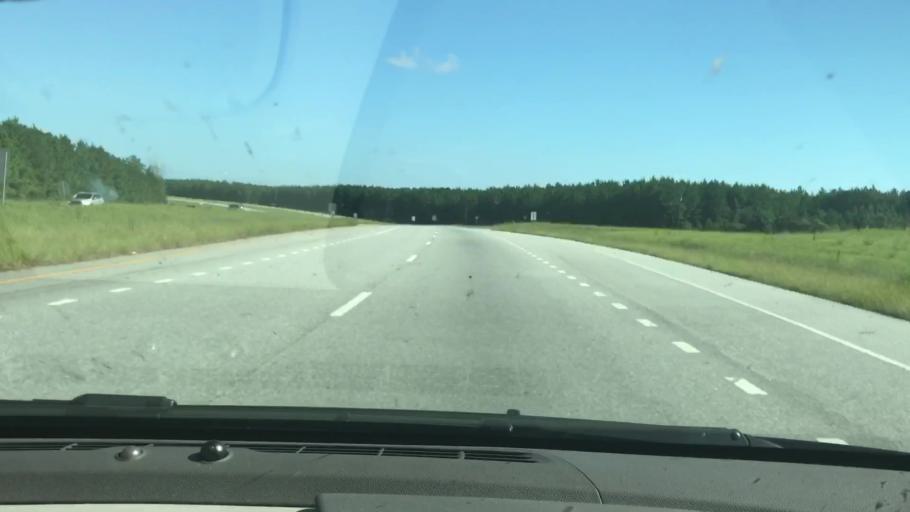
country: US
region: Alabama
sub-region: Russell County
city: Ladonia
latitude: 32.2111
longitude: -85.1693
